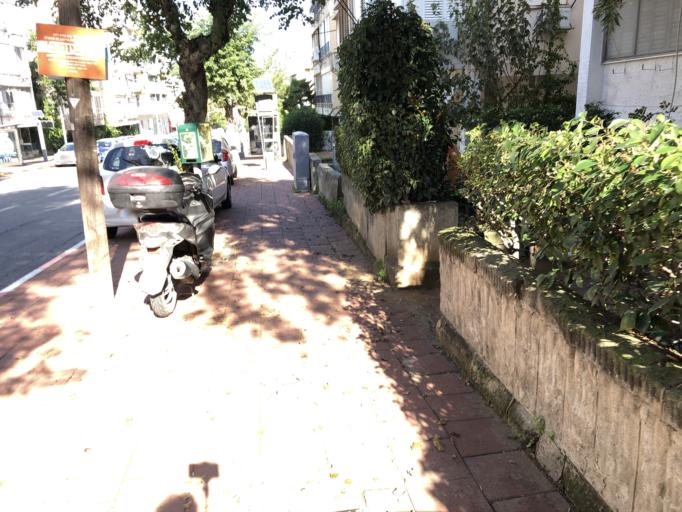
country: IL
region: Tel Aviv
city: Bene Beraq
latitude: 32.0733
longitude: 34.8250
